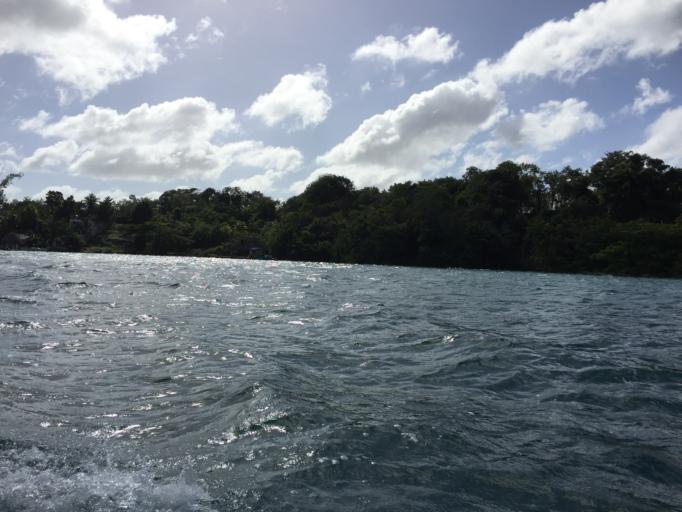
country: MX
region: Quintana Roo
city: Bacalar
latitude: 18.6503
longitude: -88.4102
